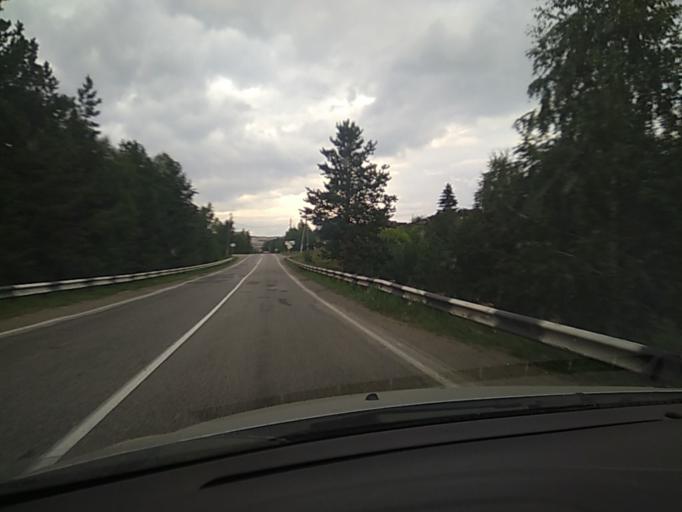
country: RU
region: Chelyabinsk
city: Kyshtym
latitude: 55.7227
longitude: 60.5128
